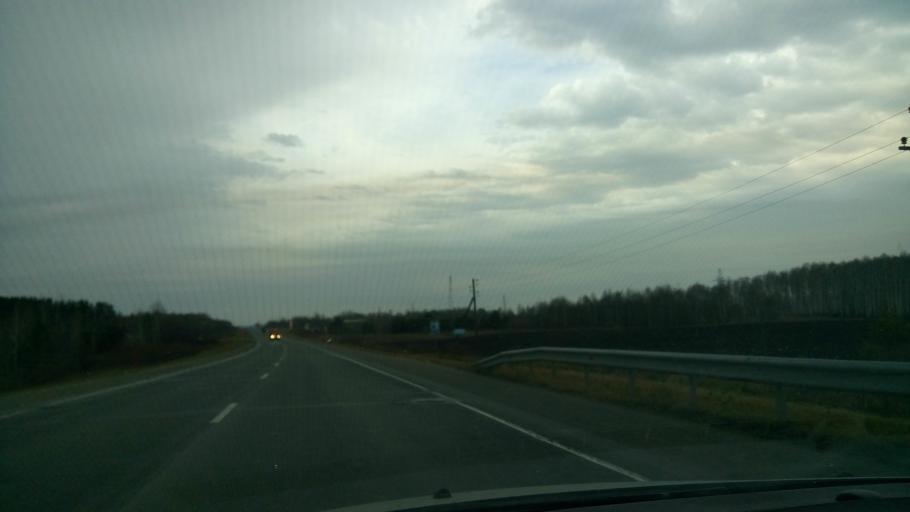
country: RU
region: Sverdlovsk
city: Obukhovskoye
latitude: 56.8539
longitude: 62.6084
